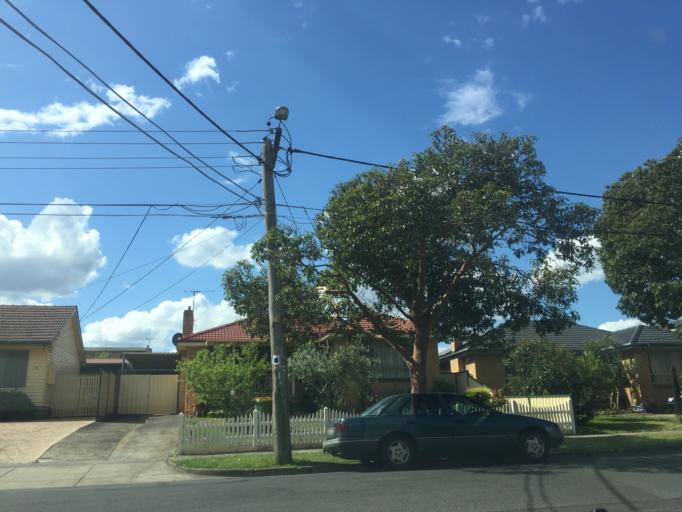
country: AU
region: Victoria
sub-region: Darebin
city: Kingsbury
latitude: -37.7146
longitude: 145.0370
